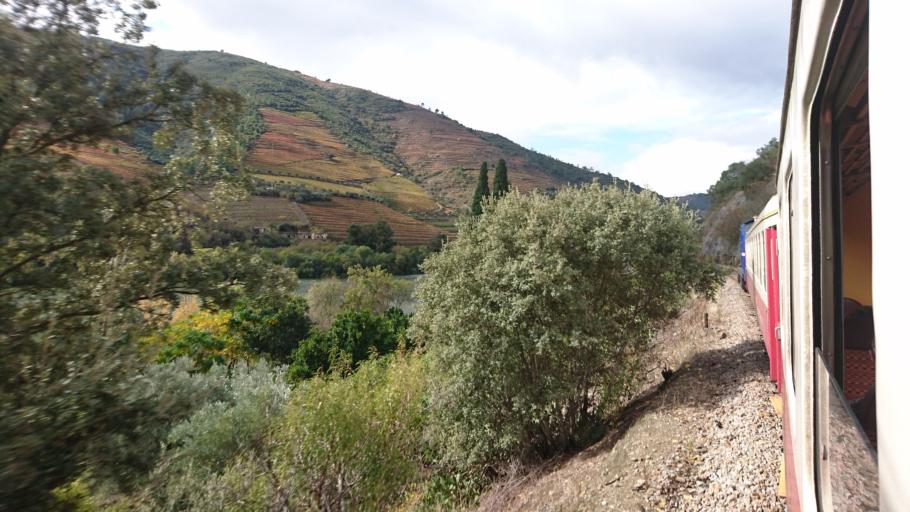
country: PT
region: Viseu
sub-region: Sao Joao da Pesqueira
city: Sao Joao da Pesqueira
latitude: 41.1999
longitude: -7.4796
